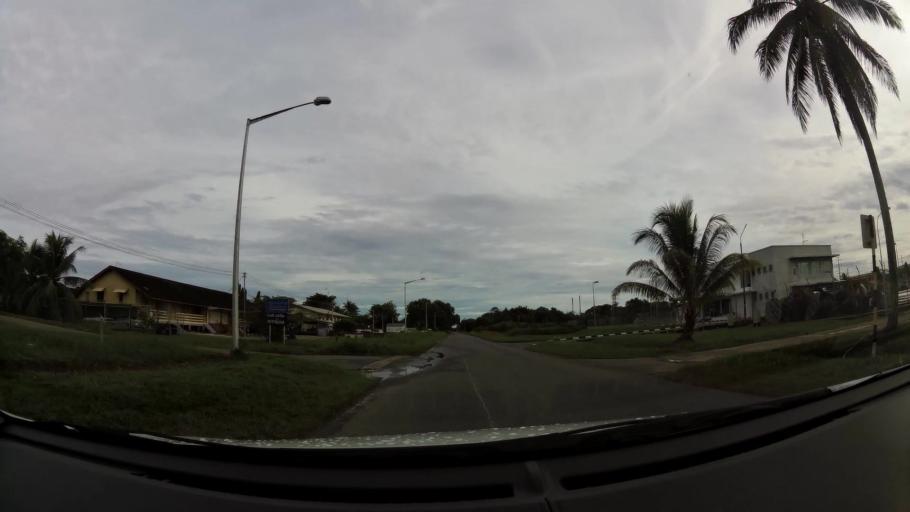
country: BN
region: Belait
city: Seria
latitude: 4.6116
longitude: 114.3396
